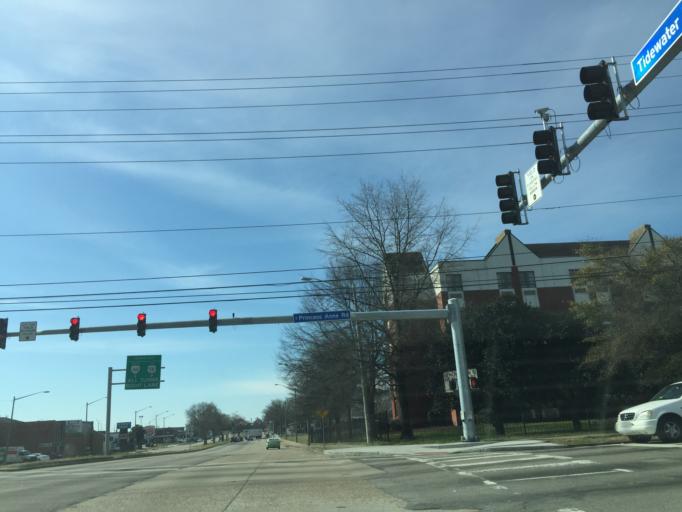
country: US
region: Virginia
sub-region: City of Norfolk
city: Norfolk
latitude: 36.8568
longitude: -76.2736
